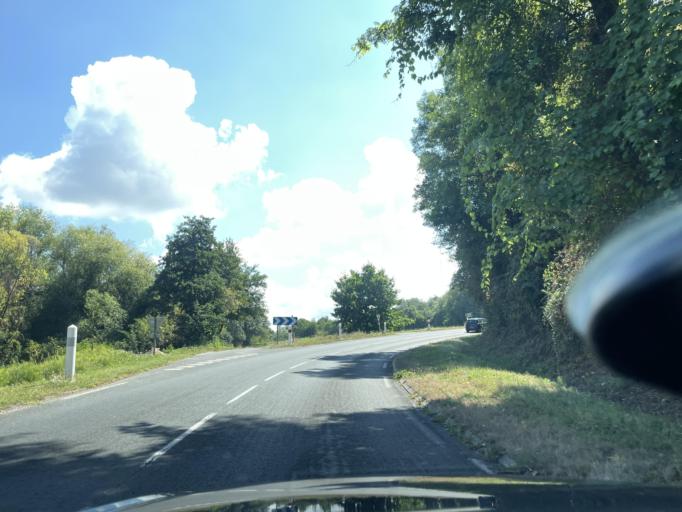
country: FR
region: Aquitaine
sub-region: Departement de la Gironde
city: Cars
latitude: 45.0781
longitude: -0.6319
